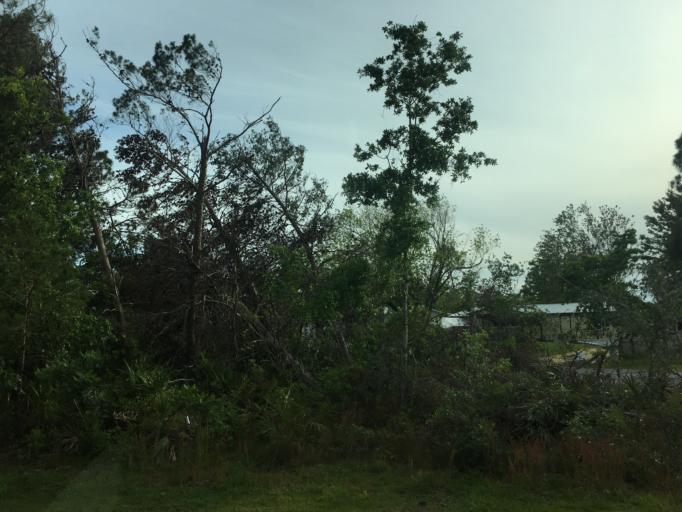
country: US
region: Florida
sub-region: Bay County
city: Upper Grand Lagoon
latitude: 30.1672
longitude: -85.7642
